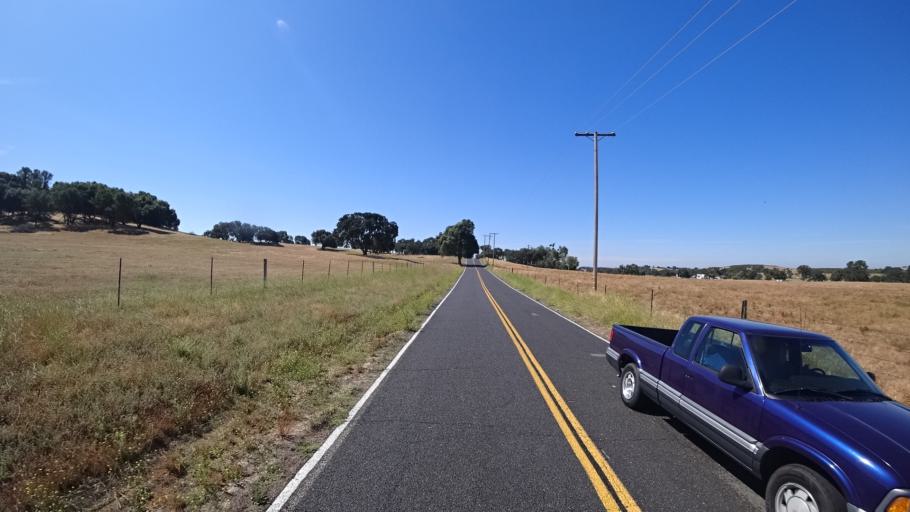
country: US
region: California
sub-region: Calaveras County
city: Rancho Calaveras
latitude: 38.1242
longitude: -120.9265
